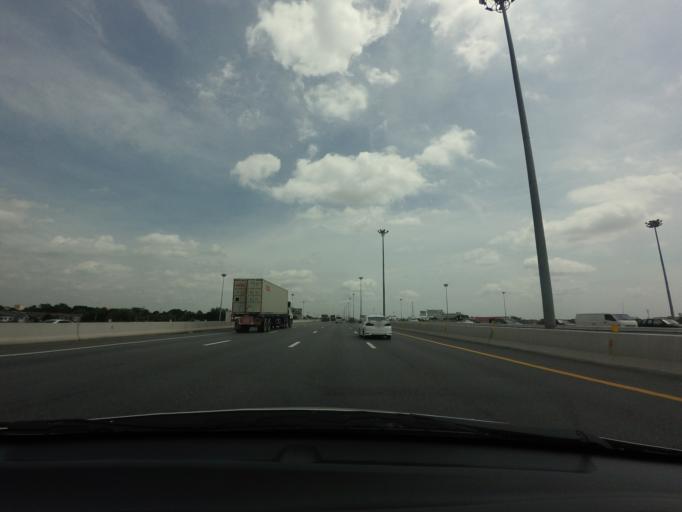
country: TH
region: Bangkok
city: Bueng Kum
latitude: 13.7915
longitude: 100.6832
